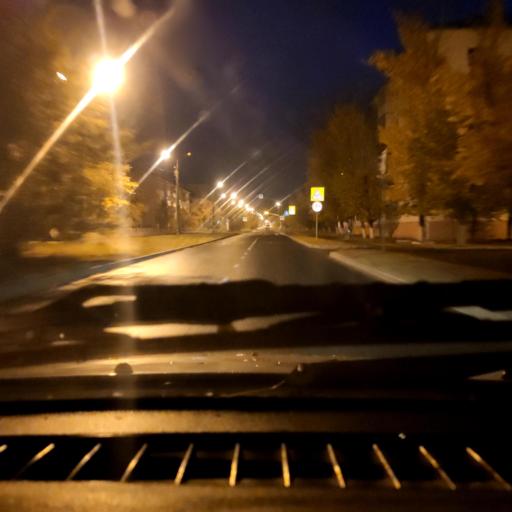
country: RU
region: Samara
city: Zhigulevsk
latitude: 53.4656
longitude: 49.5356
